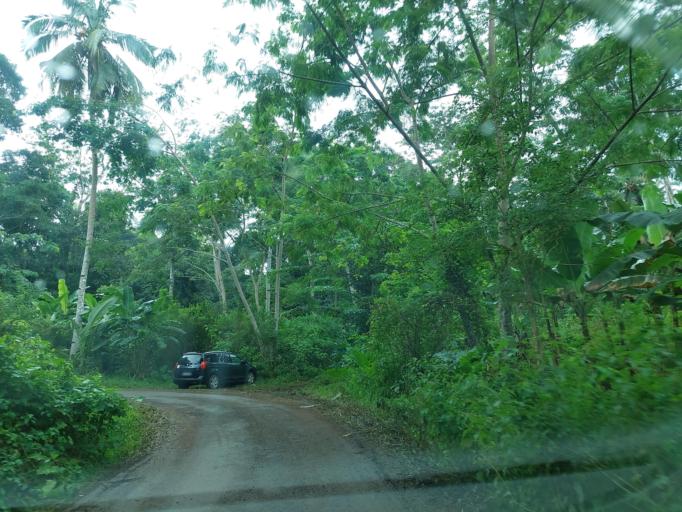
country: YT
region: Tsingoni
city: Tsingoni
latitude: -12.7647
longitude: 45.1234
